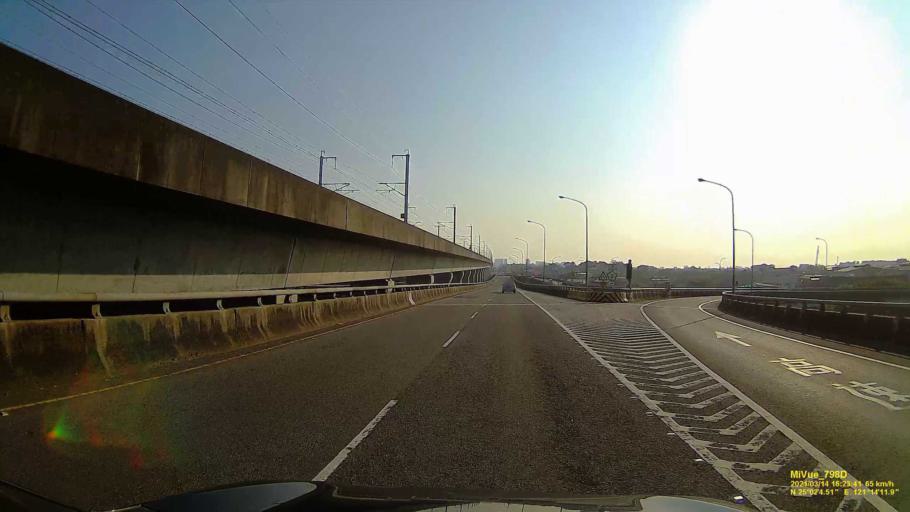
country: TW
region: Taiwan
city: Taoyuan City
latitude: 25.0344
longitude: 121.2364
